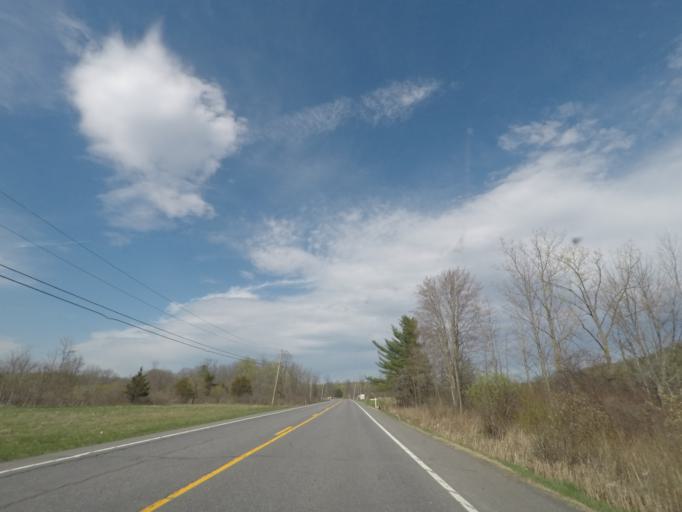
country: US
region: New York
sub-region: Albany County
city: Voorheesville
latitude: 42.5487
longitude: -73.9382
